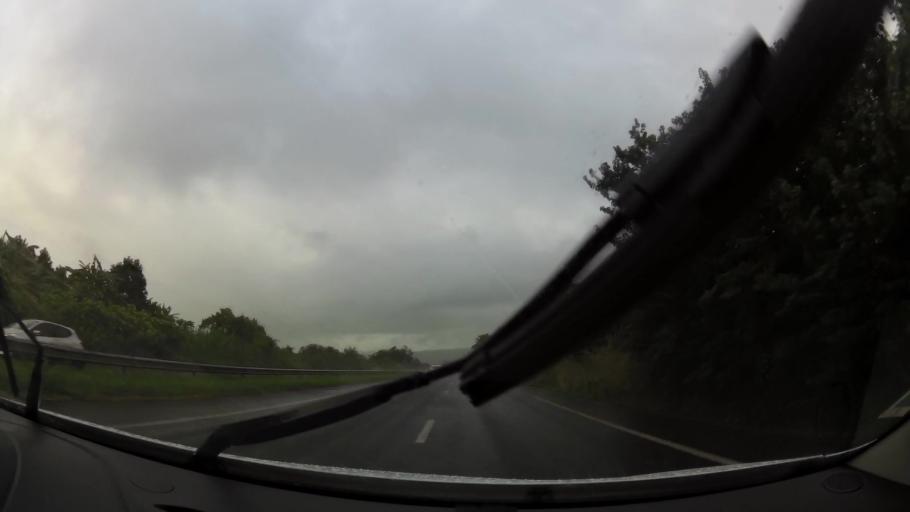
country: RE
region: Reunion
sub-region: Reunion
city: Saint-Andre
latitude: -20.9751
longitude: 55.6545
